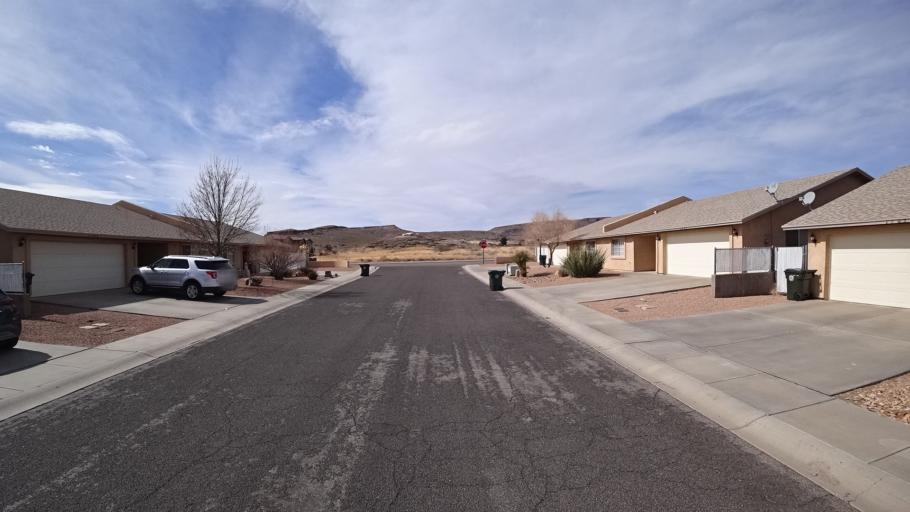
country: US
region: Arizona
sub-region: Mohave County
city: New Kingman-Butler
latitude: 35.2283
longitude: -114.0397
